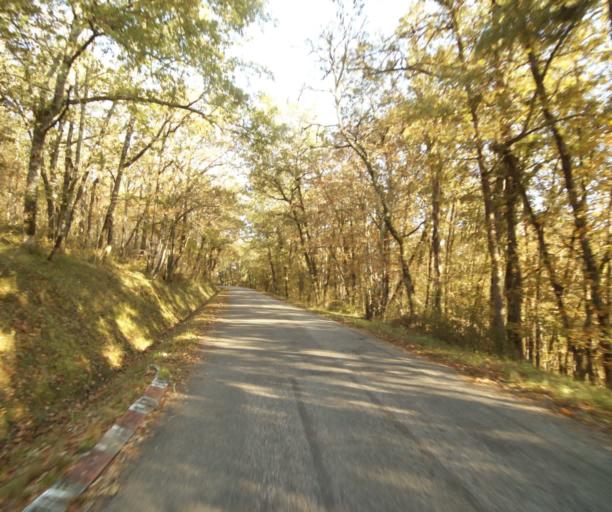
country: FR
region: Midi-Pyrenees
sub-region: Departement de la Haute-Garonne
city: Villemur-sur-Tarn
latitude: 43.8903
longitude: 1.4984
